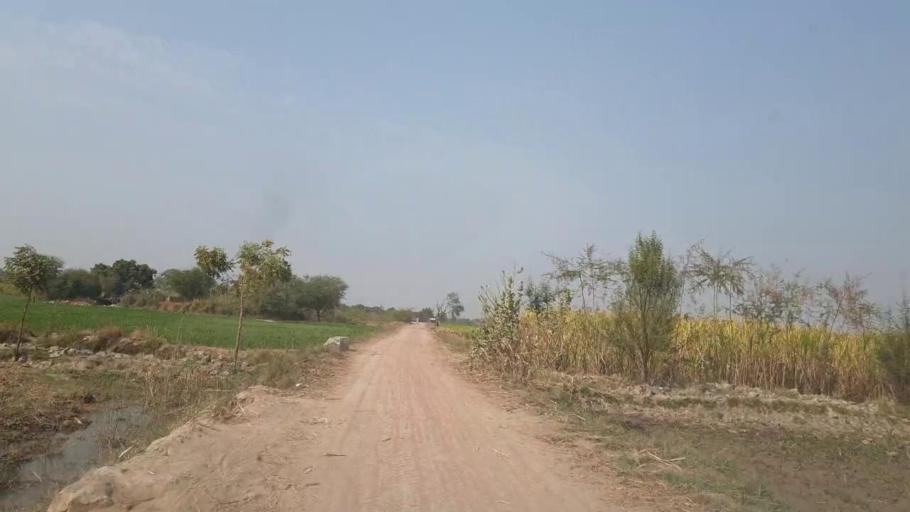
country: PK
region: Sindh
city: Mirpur Khas
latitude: 25.5782
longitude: 69.1360
